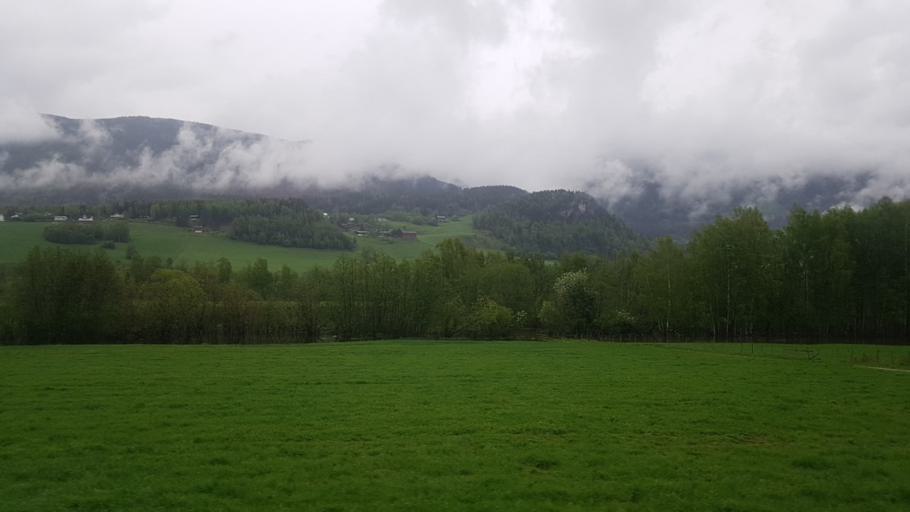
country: NO
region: Oppland
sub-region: Ringebu
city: Ringebu
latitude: 61.4361
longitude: 10.2037
